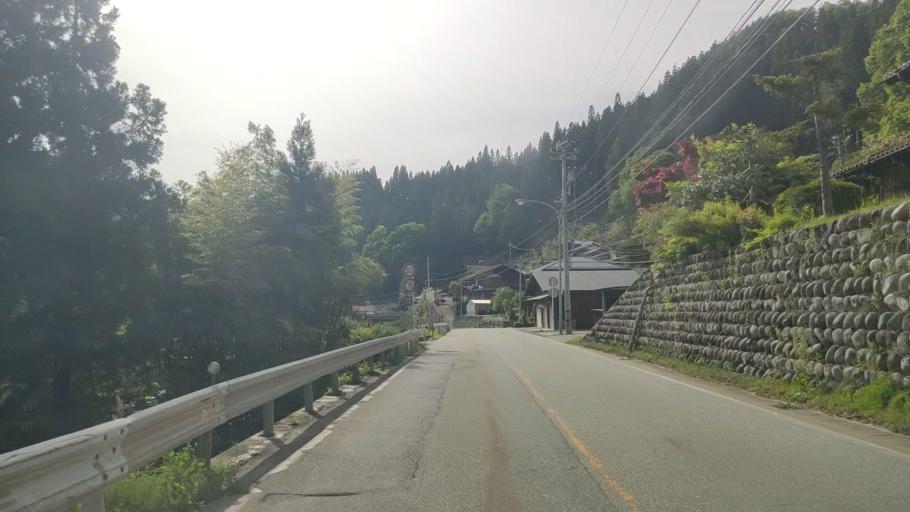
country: JP
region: Gifu
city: Takayama
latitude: 36.3017
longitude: 137.3417
